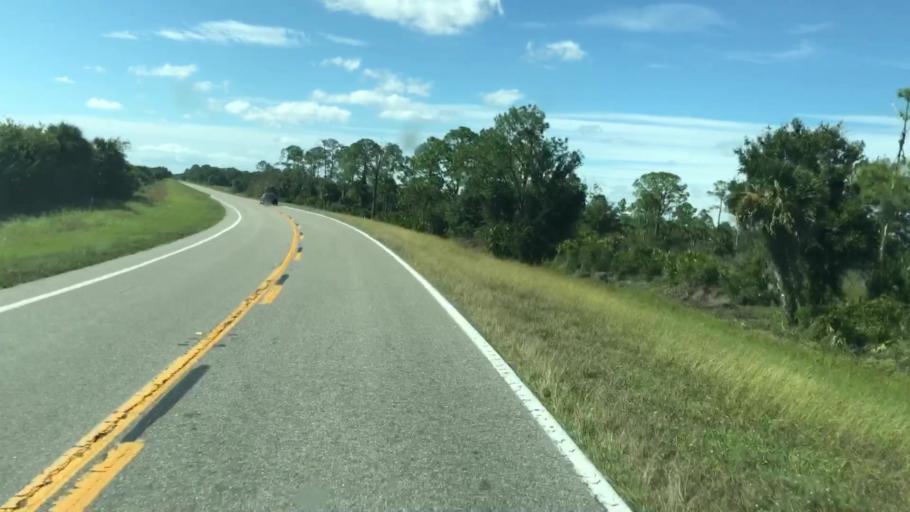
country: US
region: Florida
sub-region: Lee County
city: Olga
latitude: 26.7399
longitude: -81.7162
